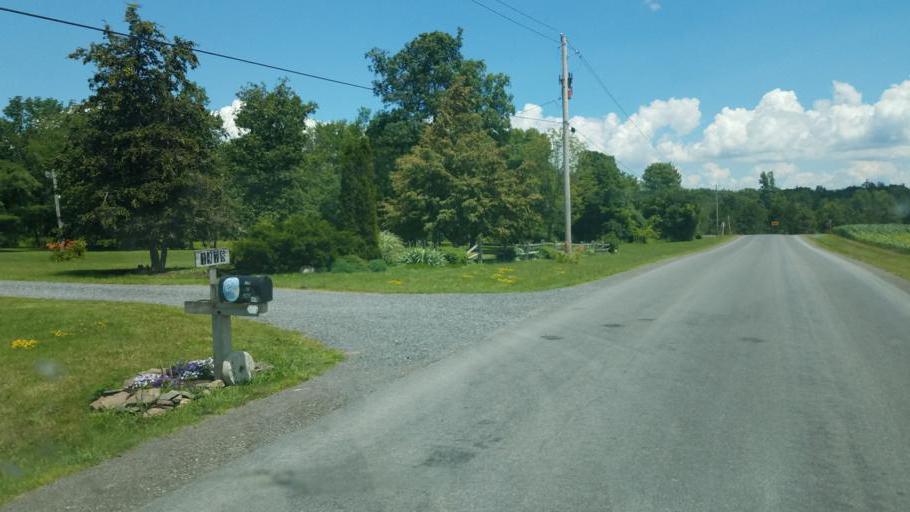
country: US
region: New York
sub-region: Yates County
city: Dundee
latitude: 42.5936
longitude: -77.0043
